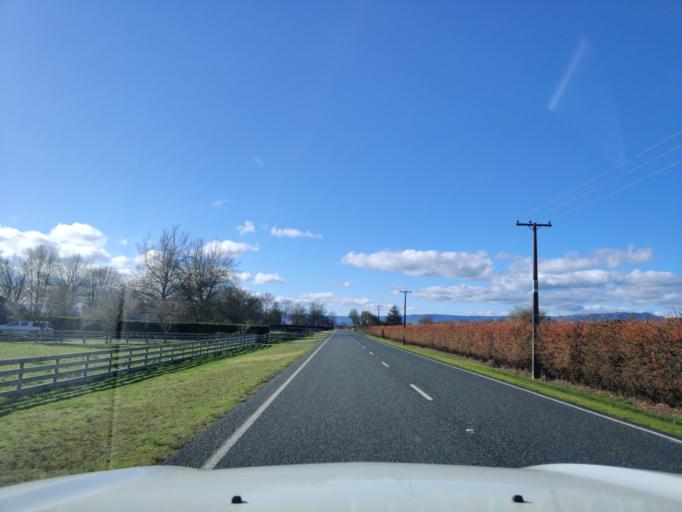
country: NZ
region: Waikato
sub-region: Matamata-Piako District
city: Matamata
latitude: -37.8700
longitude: 175.7471
